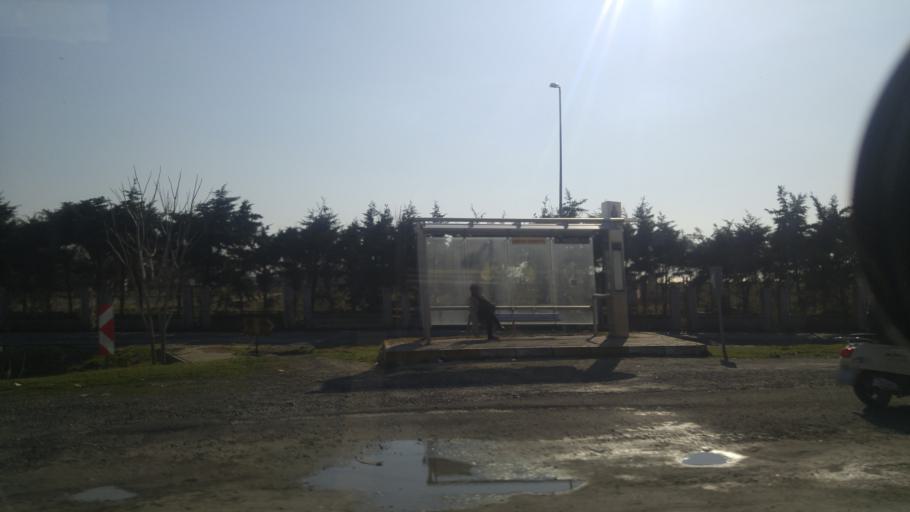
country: TR
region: Istanbul
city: Selimpasa
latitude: 41.0534
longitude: 28.3796
